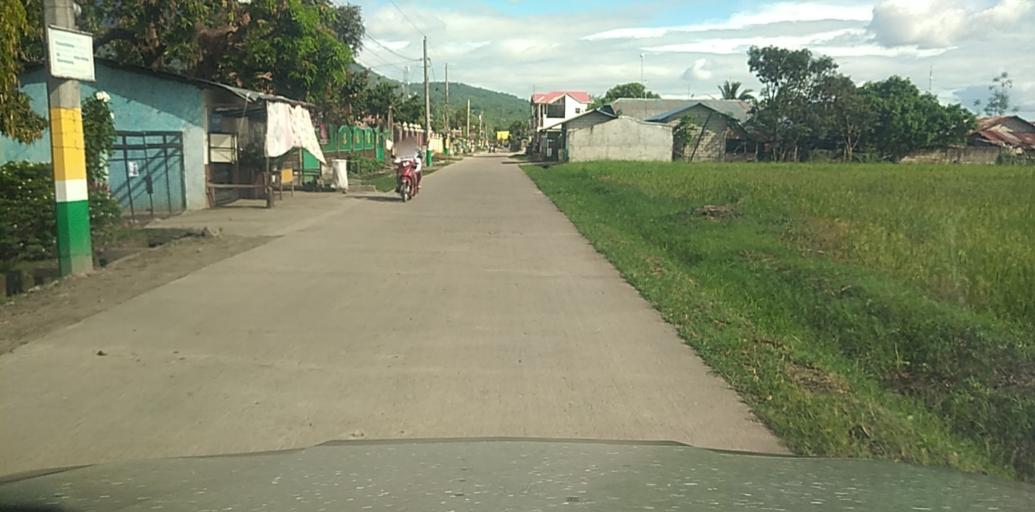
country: PH
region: Central Luzon
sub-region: Province of Pampanga
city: Buensuseso
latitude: 15.1921
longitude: 120.6857
